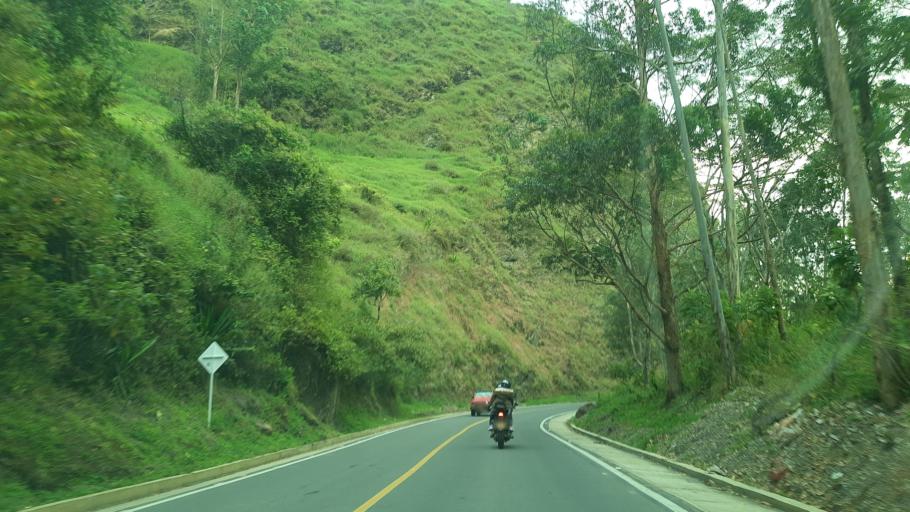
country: CO
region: Boyaca
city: Somondoco
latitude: 5.0103
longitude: -73.3980
